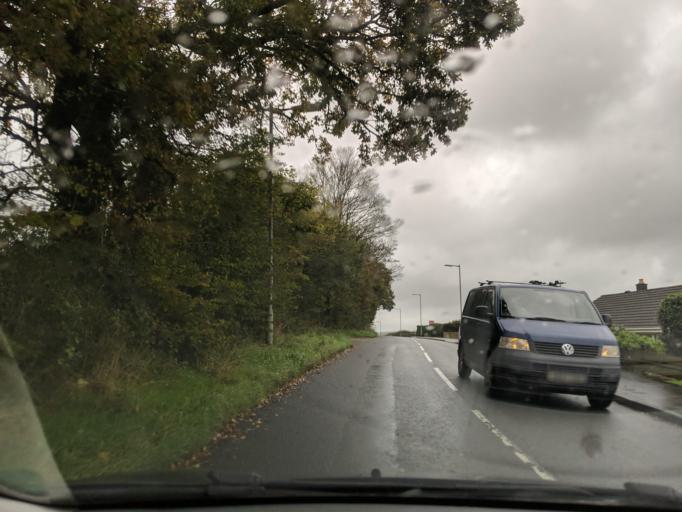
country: GB
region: England
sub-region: Cornwall
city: Bodmin
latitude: 50.4659
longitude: -4.7205
